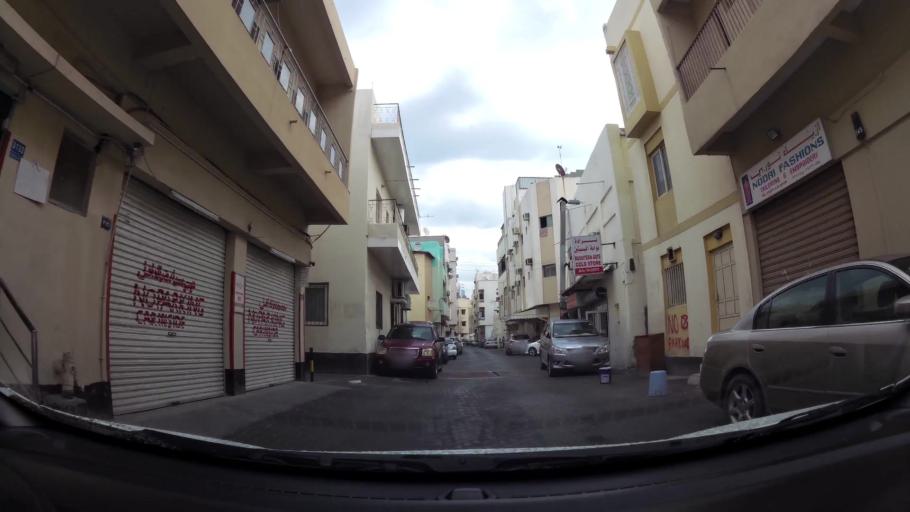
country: BH
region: Manama
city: Manama
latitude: 26.2310
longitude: 50.5918
